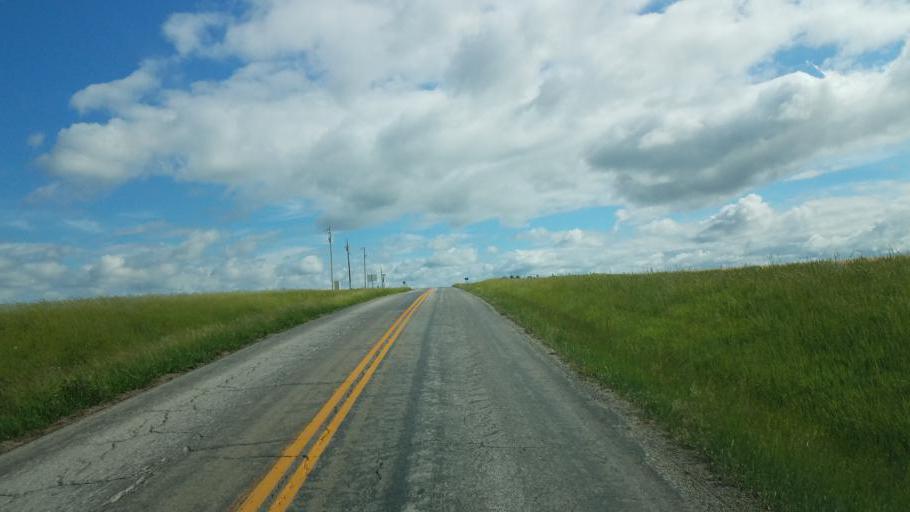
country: US
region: Missouri
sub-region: Mercer County
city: Princeton
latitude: 40.2651
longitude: -93.6757
